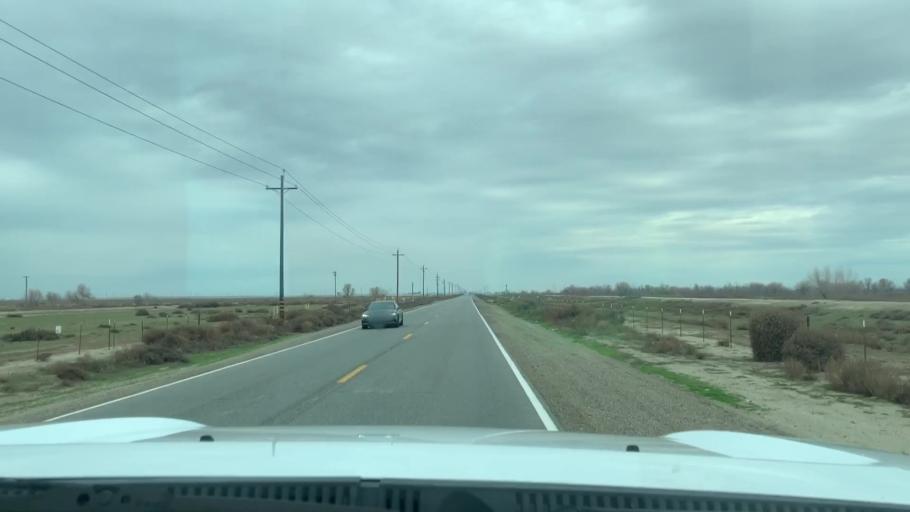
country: US
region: California
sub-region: Kern County
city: Rosedale
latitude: 35.3302
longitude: -119.2524
